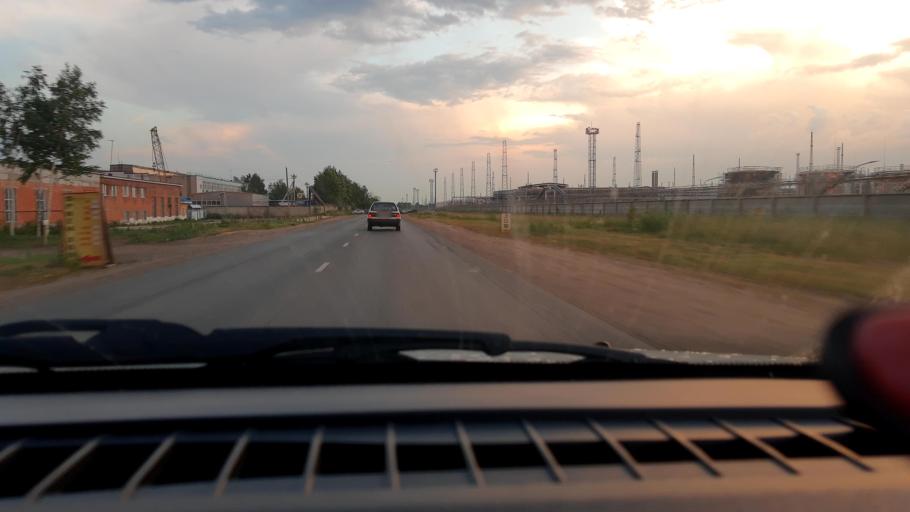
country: RU
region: Nizjnij Novgorod
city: Kstovo
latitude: 56.1233
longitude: 44.1304
